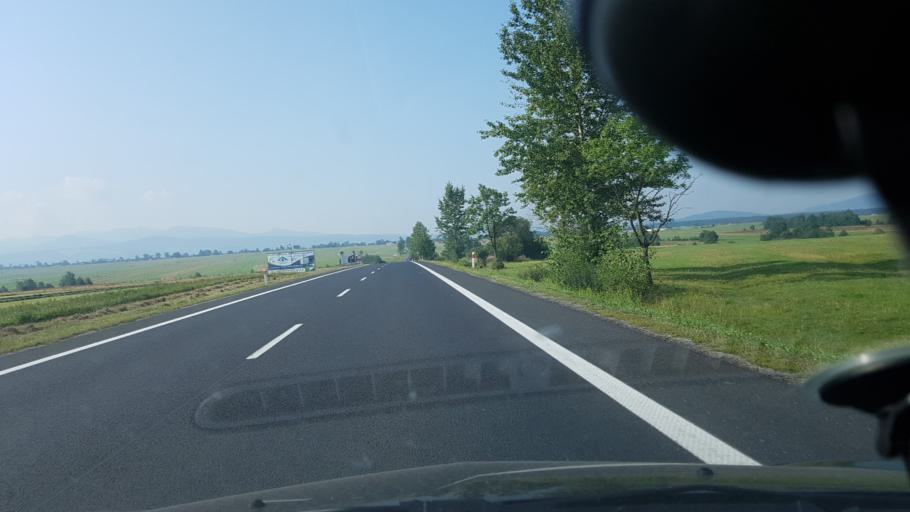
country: PL
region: Lesser Poland Voivodeship
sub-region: Powiat nowotarski
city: Chyzne
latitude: 49.4456
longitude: 19.6844
